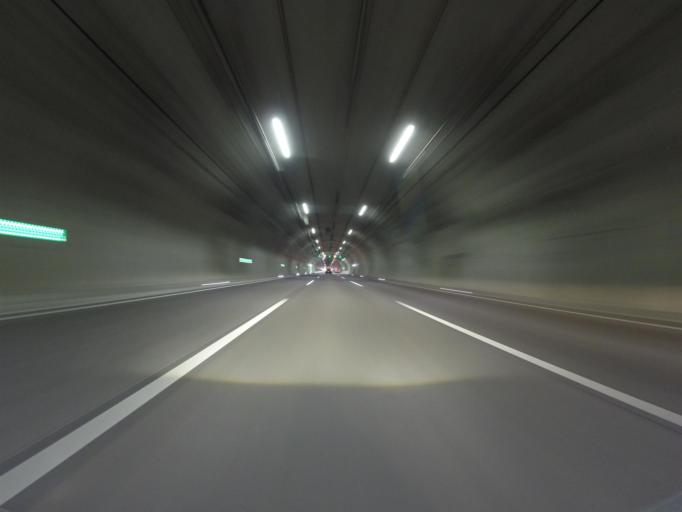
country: DE
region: Thuringia
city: Rothenstein
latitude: 50.8742
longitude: 11.5623
